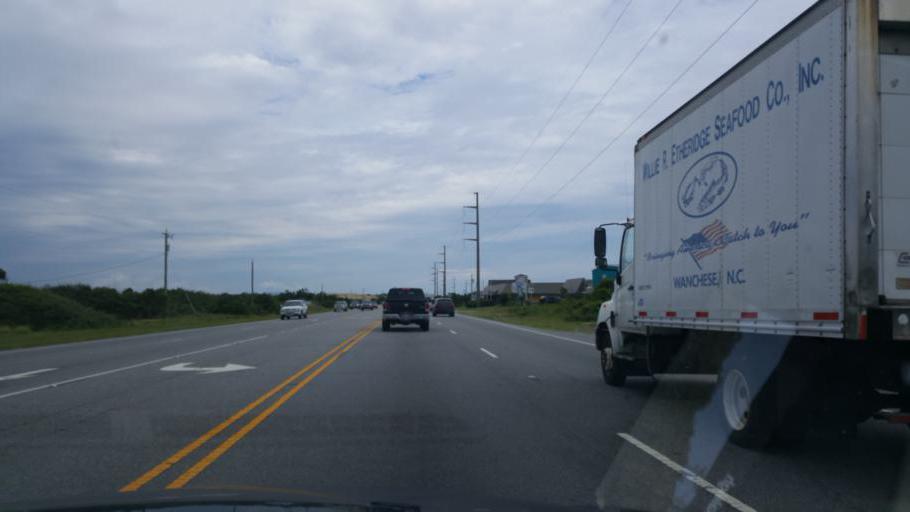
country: US
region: North Carolina
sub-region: Dare County
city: Nags Head
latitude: 35.9515
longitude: -75.6228
